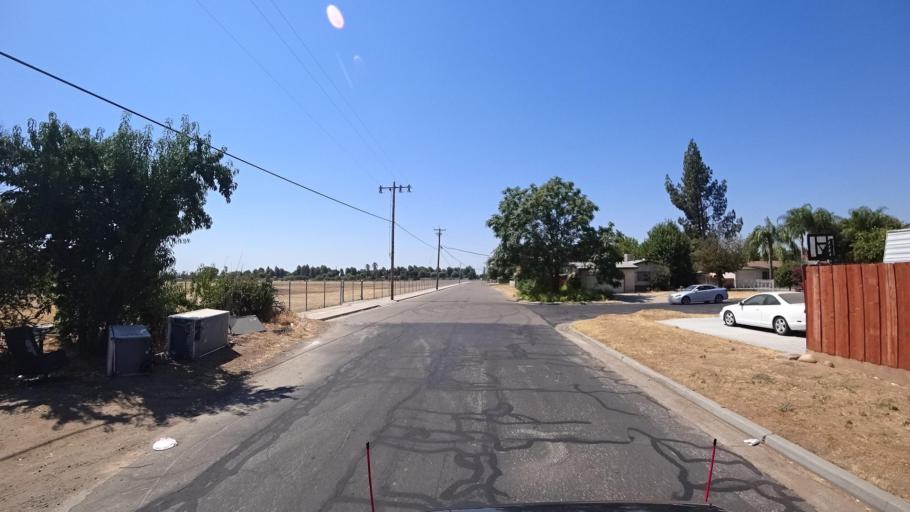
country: US
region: California
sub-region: Fresno County
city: Sunnyside
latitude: 36.7567
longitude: -119.7093
